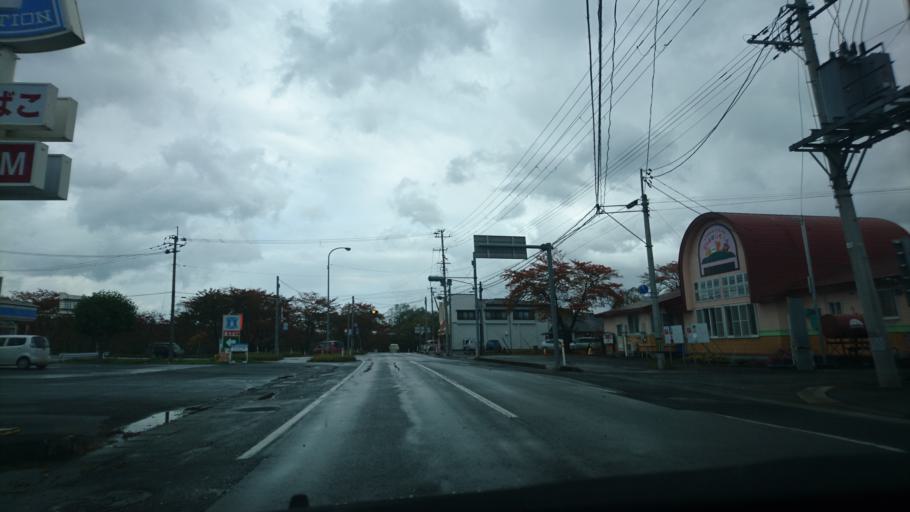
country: JP
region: Iwate
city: Shizukuishi
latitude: 39.6630
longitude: 140.9694
